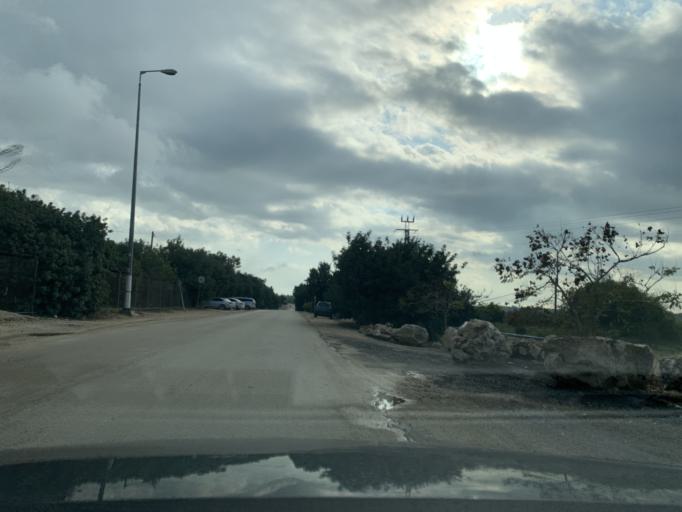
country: IL
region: Central District
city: Rosh Ha'Ayin
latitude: 32.0664
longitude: 34.9471
